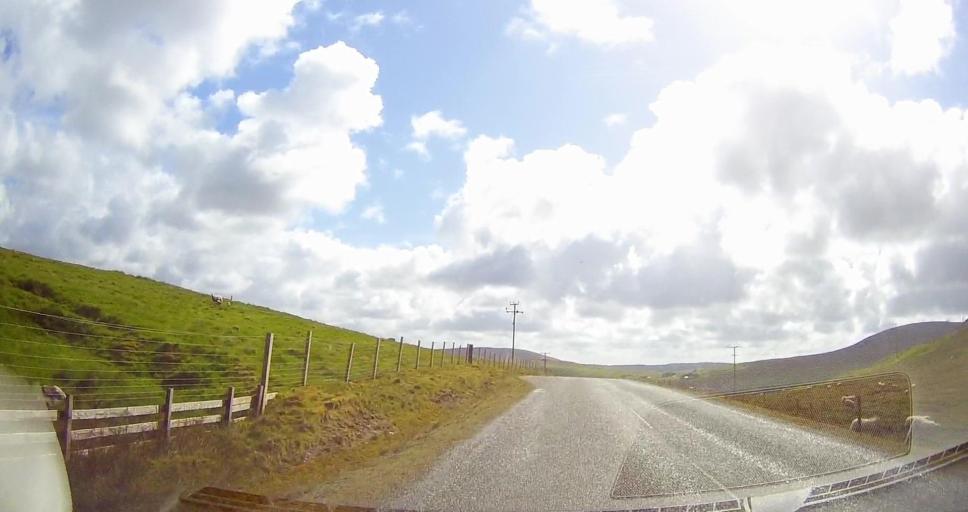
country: GB
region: Scotland
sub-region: Shetland Islands
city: Lerwick
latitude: 60.5428
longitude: -1.3428
